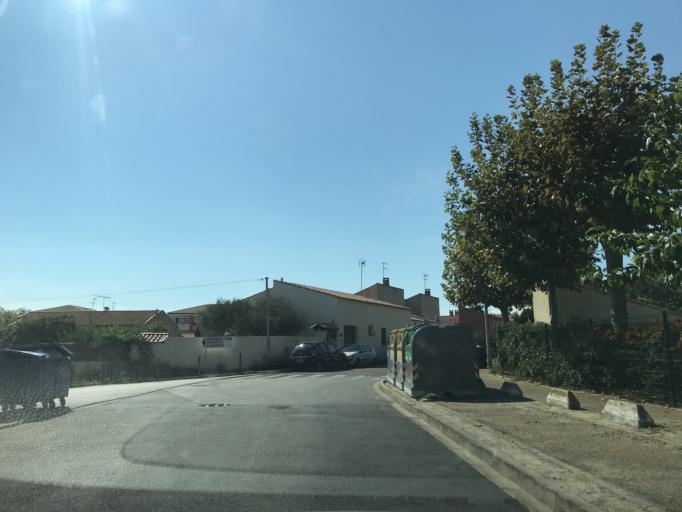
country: FR
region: Languedoc-Roussillon
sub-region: Departement du Gard
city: Le Grau-du-Roi
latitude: 43.5258
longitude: 4.1470
